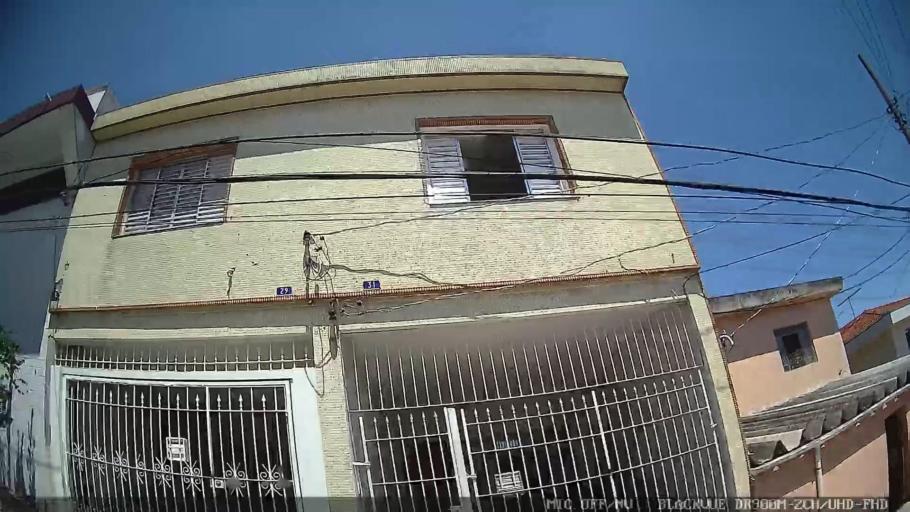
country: BR
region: Sao Paulo
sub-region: Sao Caetano Do Sul
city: Sao Caetano do Sul
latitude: -23.5970
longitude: -46.5421
